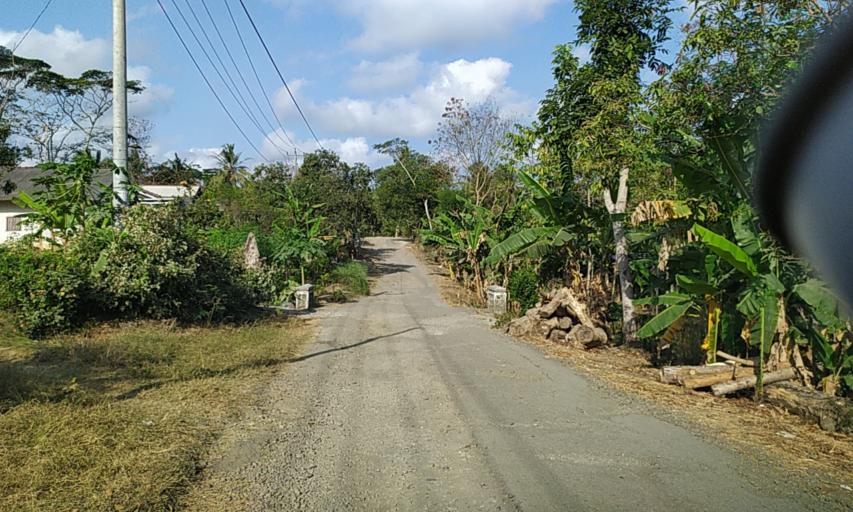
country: ID
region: Central Java
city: Jeruklegi
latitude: -7.6473
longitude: 108.9653
